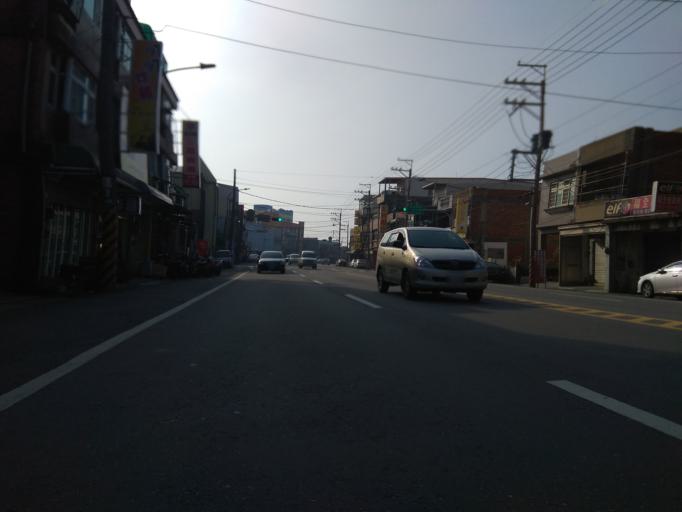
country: TW
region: Taiwan
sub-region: Hsinchu
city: Zhubei
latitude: 24.9705
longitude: 121.1179
